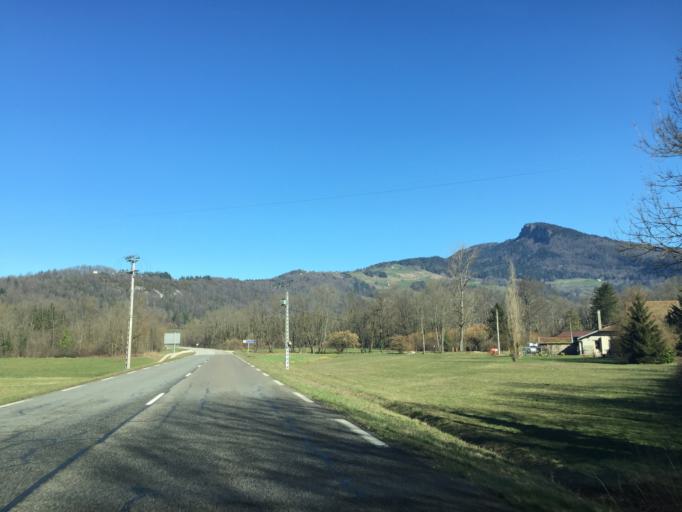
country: FR
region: Rhone-Alpes
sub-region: Departement de la Savoie
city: Les Echelles
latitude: 45.4379
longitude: 5.7655
